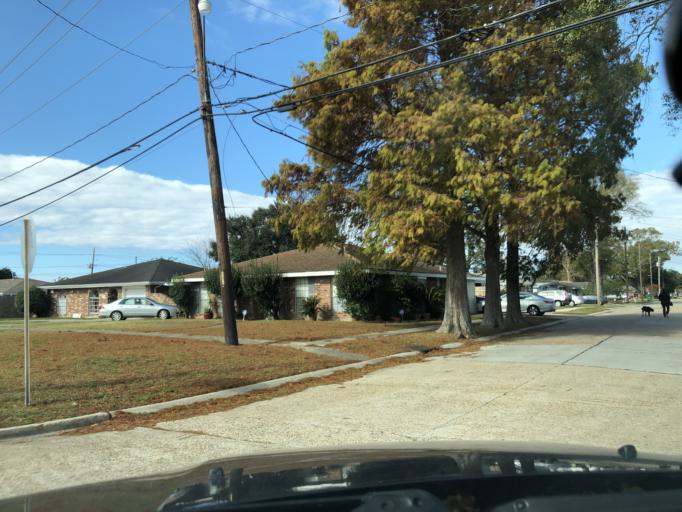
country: US
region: Louisiana
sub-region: Jefferson Parish
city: Metairie Terrace
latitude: 29.9821
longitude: -90.1693
